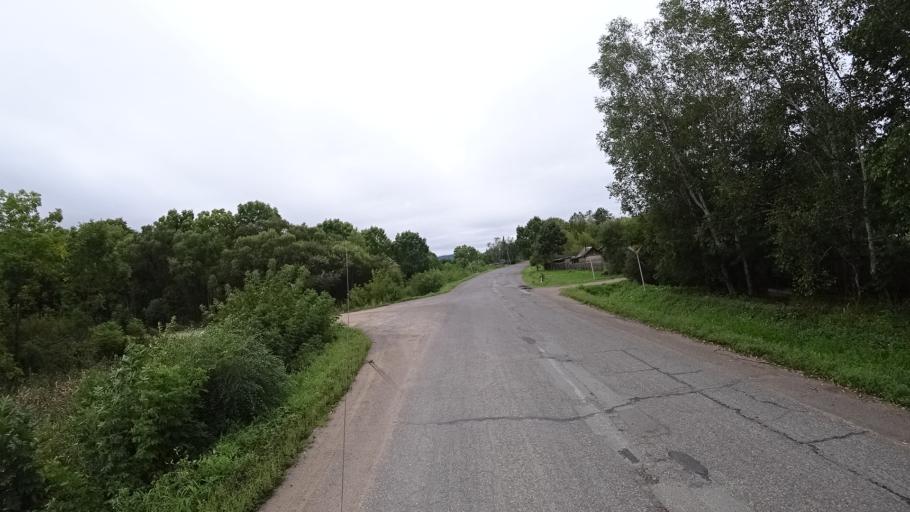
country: RU
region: Primorskiy
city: Rettikhovka
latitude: 44.1674
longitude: 132.7418
